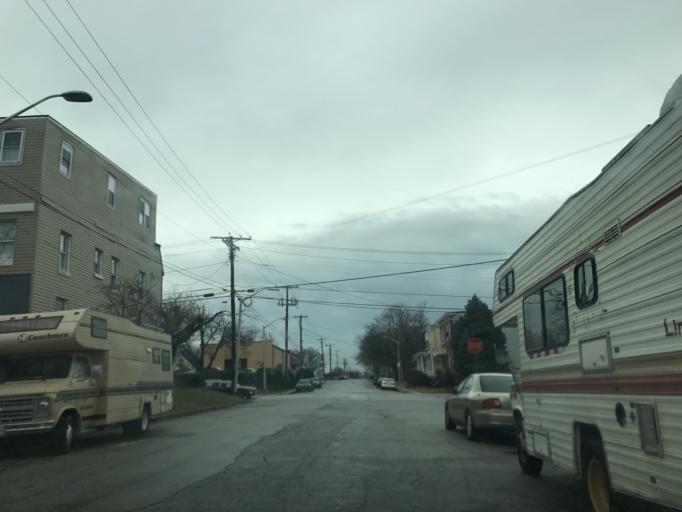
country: US
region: Maryland
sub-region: Baltimore County
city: Rosedale
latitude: 39.3032
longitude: -76.5600
